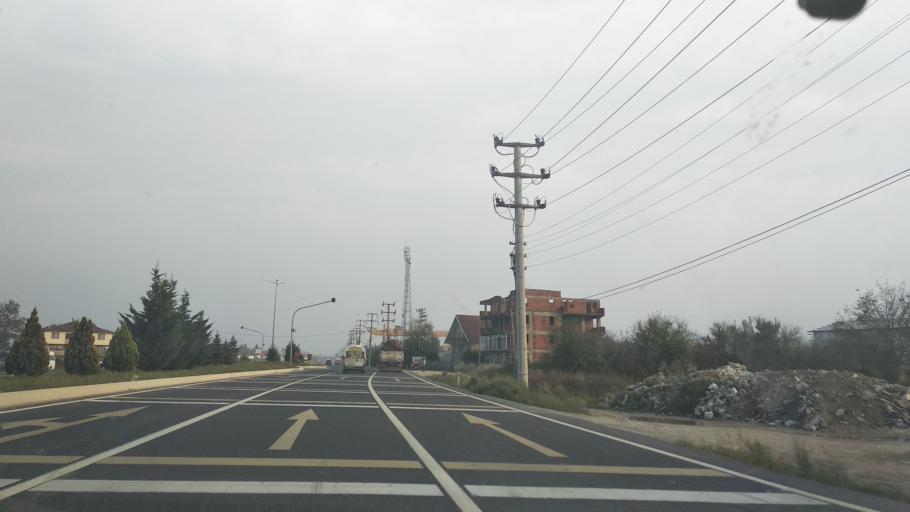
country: TR
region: Duzce
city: Duzce
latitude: 40.8122
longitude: 31.2204
